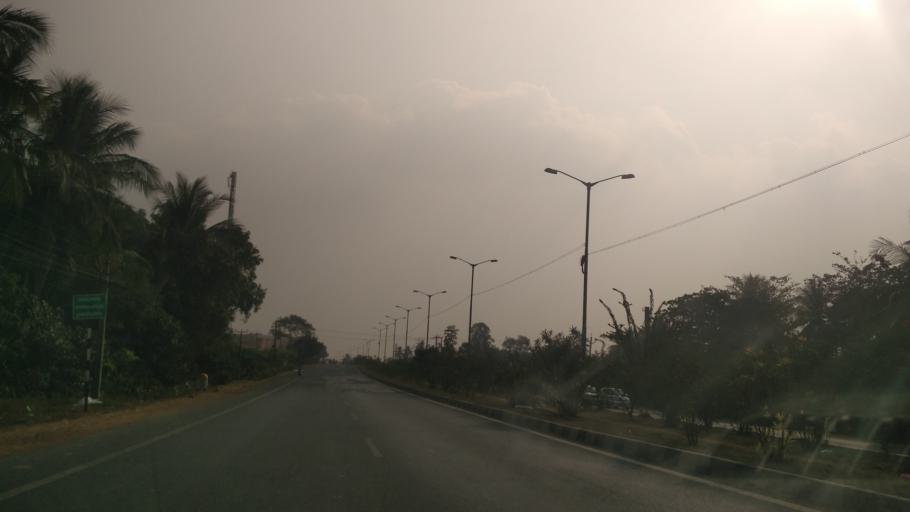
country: IN
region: Andhra Pradesh
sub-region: East Godavari
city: Rajahmundry
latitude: 16.9596
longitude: 81.7942
